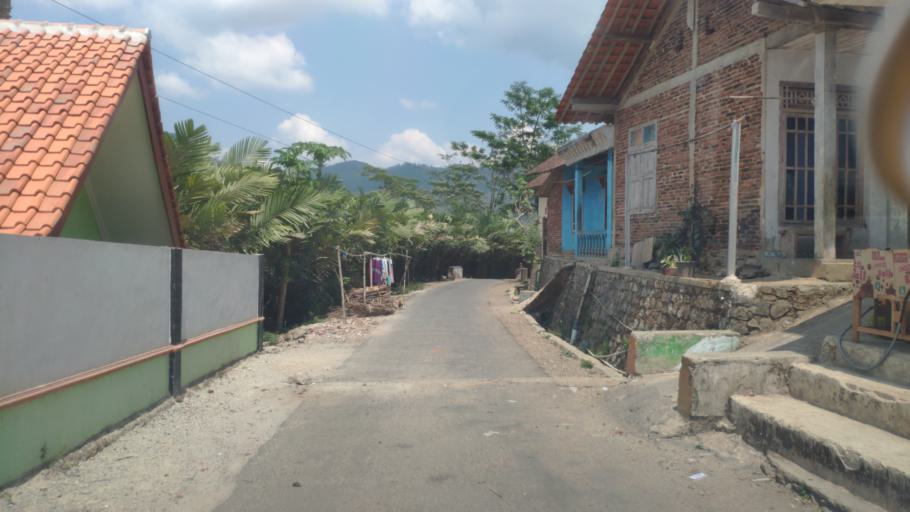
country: ID
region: Central Java
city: Wonosobo
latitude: -7.3144
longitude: 109.6499
